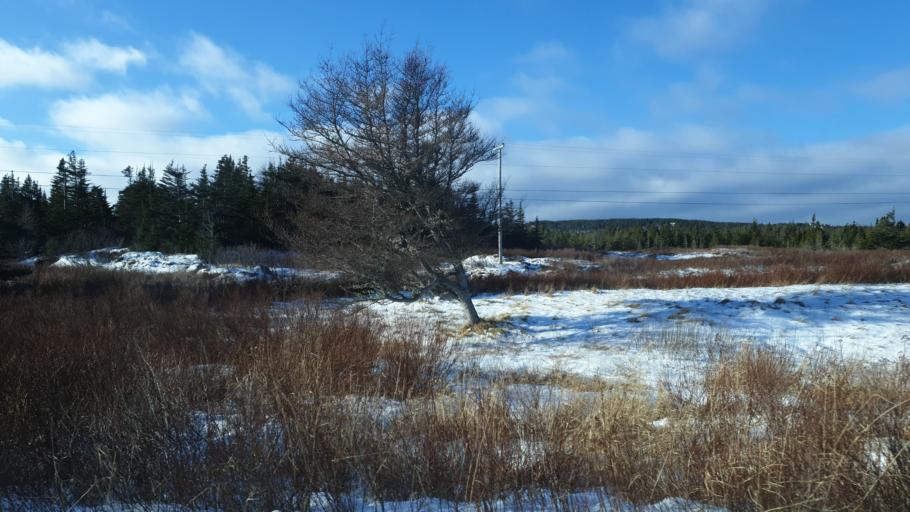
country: CA
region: Newfoundland and Labrador
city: Bonavista
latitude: 48.6260
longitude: -53.0342
